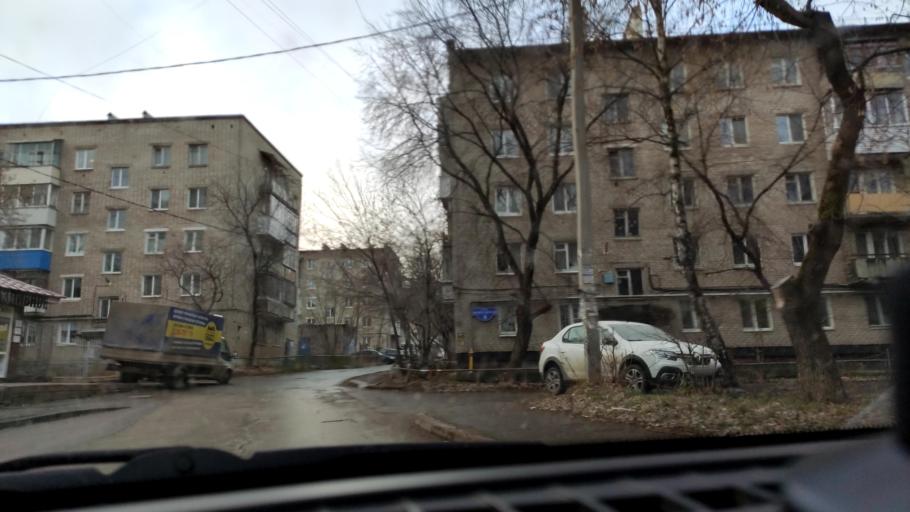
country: RU
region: Perm
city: Perm
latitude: 58.0029
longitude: 56.2775
